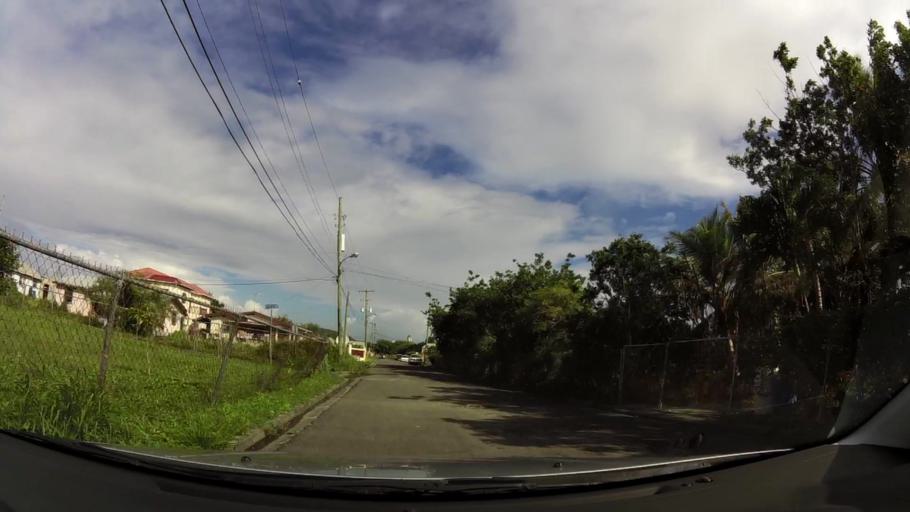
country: AG
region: Saint George
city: Piggotts
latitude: 17.1210
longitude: -61.8200
